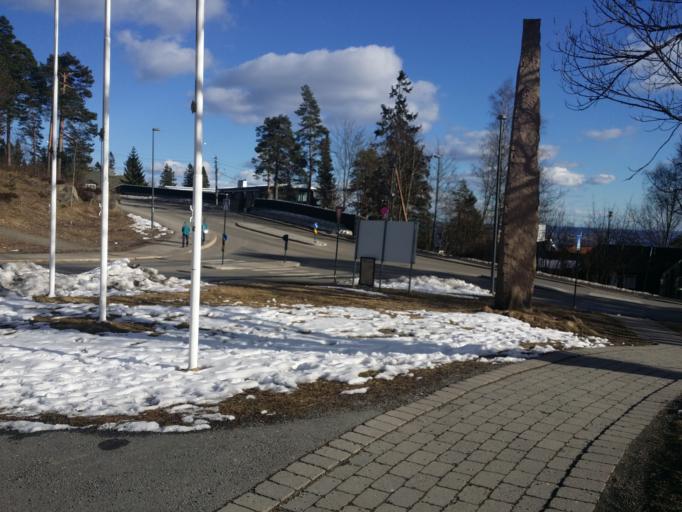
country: NO
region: Oslo
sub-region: Oslo
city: Sjolyststranda
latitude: 59.9616
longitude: 10.6667
